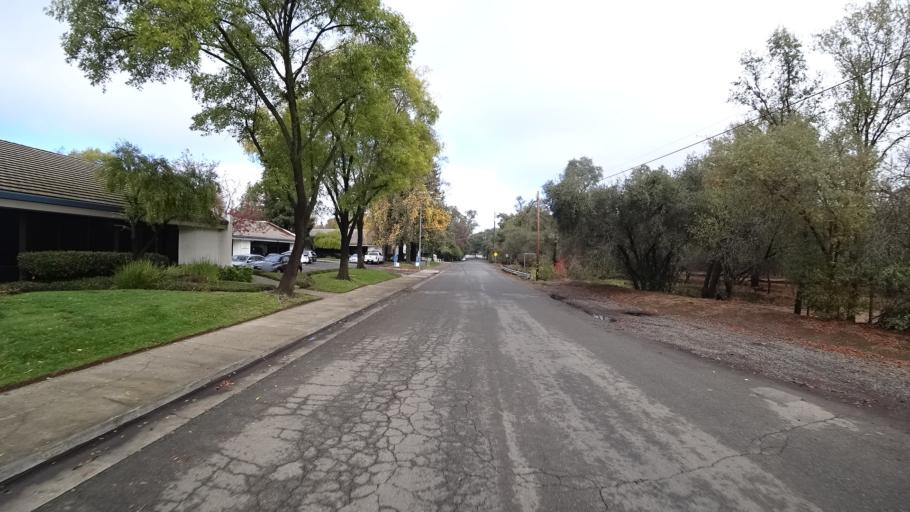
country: US
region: California
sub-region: Sacramento County
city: Antelope
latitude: 38.6813
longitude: -121.3222
